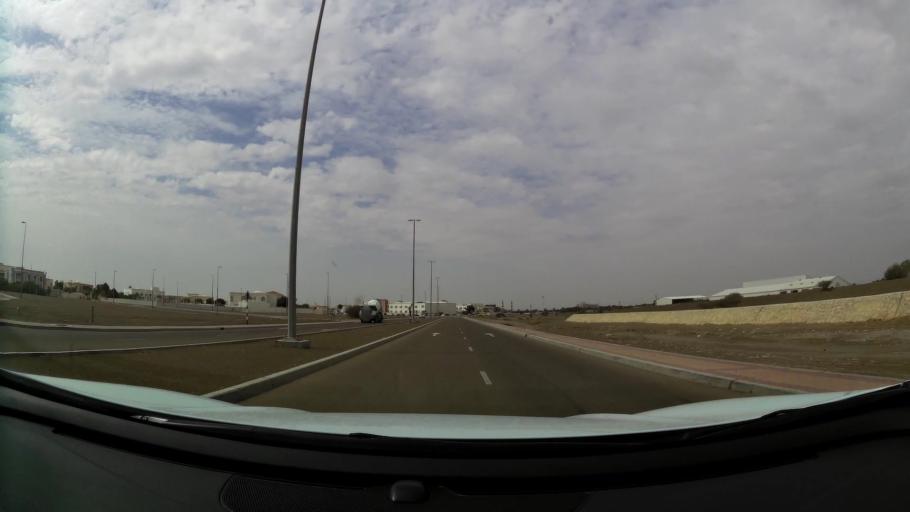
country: AE
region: Abu Dhabi
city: Al Ain
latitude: 24.1971
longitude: 55.8117
